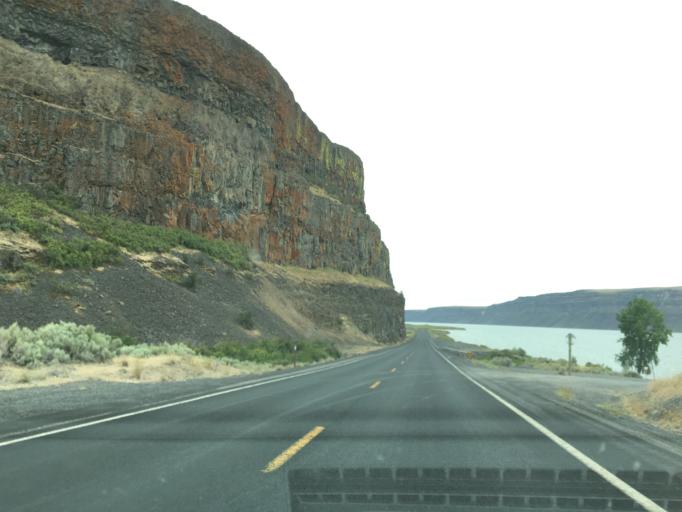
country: US
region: Washington
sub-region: Okanogan County
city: Coulee Dam
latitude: 47.7199
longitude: -119.2569
